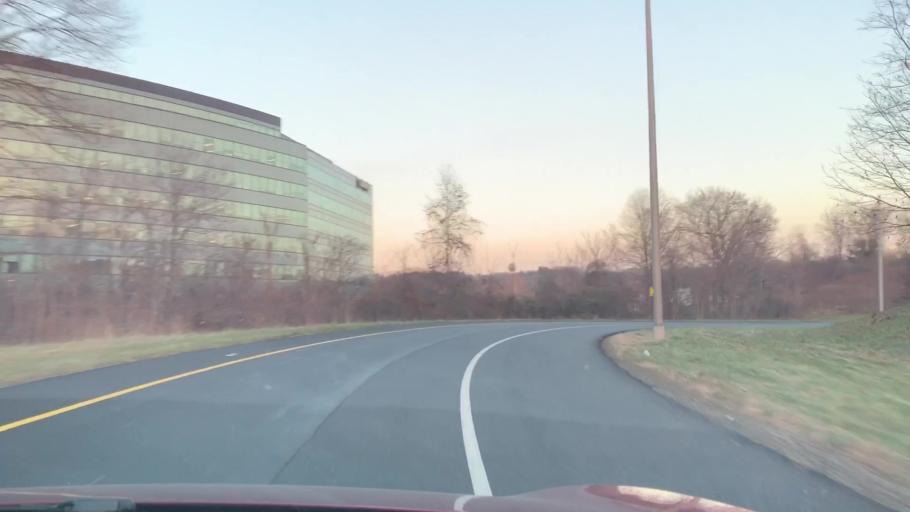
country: US
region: Connecticut
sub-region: Fairfield County
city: Norwalk
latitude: 41.1434
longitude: -73.4301
